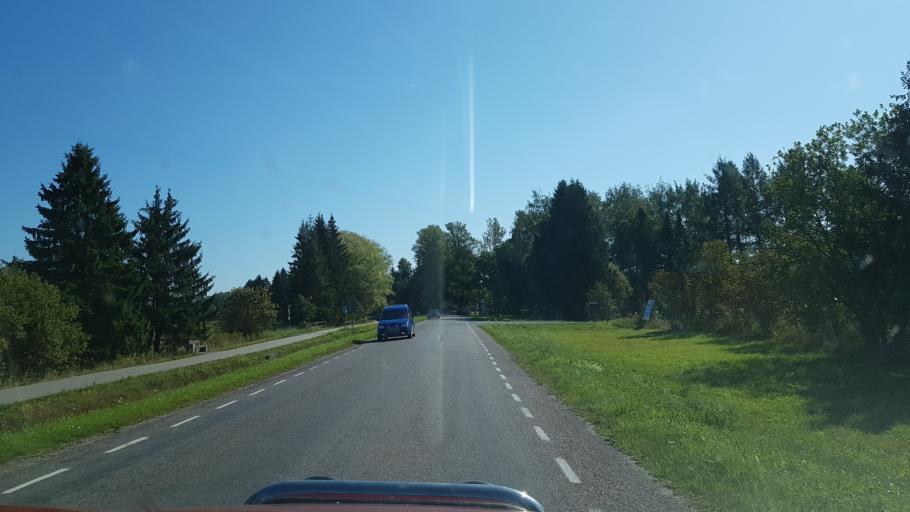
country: EE
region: Tartu
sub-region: Tartu linn
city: Tartu
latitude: 58.3567
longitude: 26.8695
